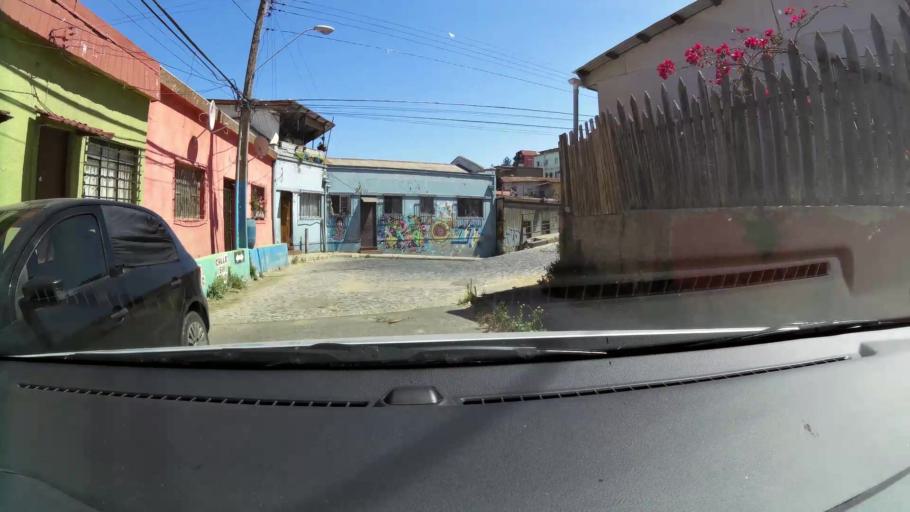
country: CL
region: Valparaiso
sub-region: Provincia de Valparaiso
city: Valparaiso
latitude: -33.0518
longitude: -71.5994
